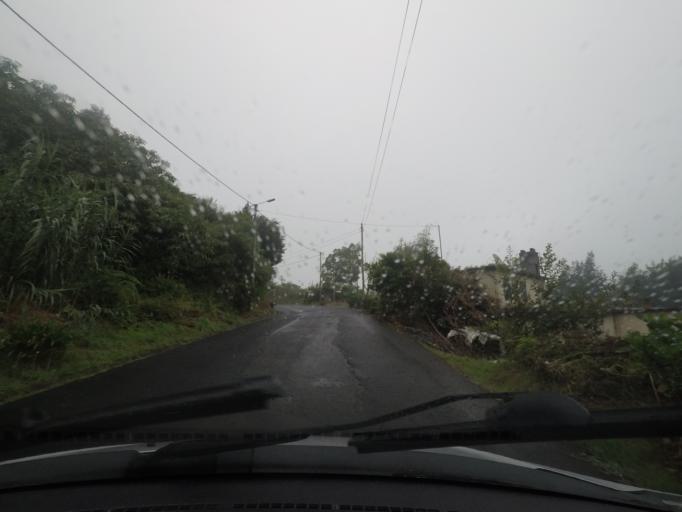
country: PT
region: Madeira
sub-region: Santana
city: Santana
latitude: 32.7958
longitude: -16.8781
